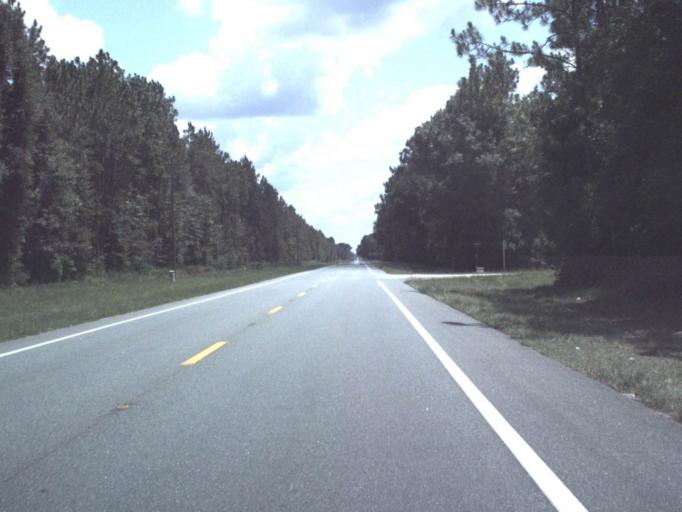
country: US
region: Florida
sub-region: Alachua County
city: High Springs
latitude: 29.8036
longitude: -82.7412
